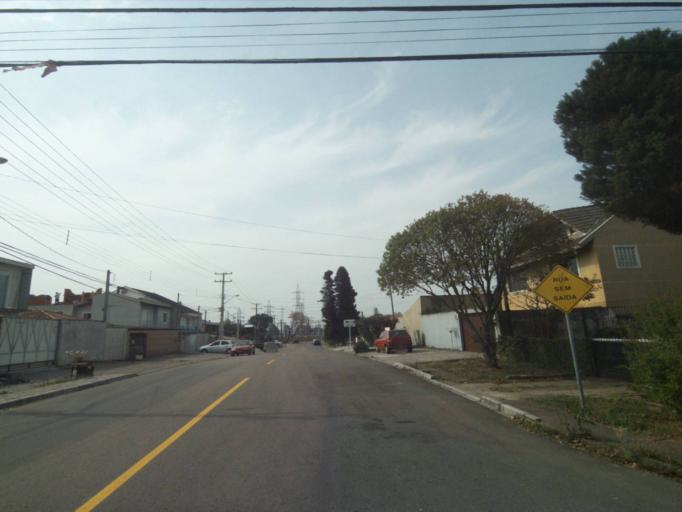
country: BR
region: Parana
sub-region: Pinhais
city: Pinhais
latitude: -25.4801
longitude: -49.2095
